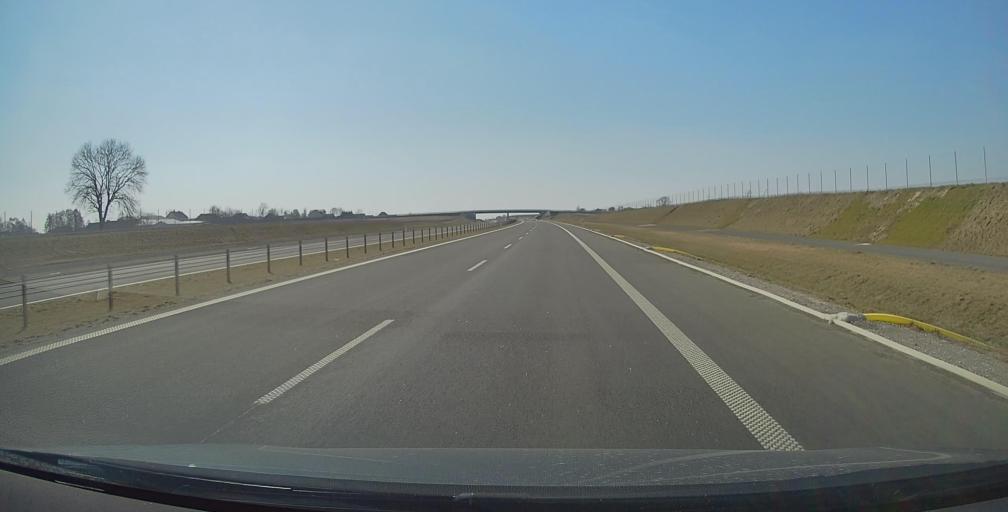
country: PL
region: Lublin Voivodeship
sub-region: Powiat janowski
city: Modliborzyce
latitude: 50.7961
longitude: 22.2940
